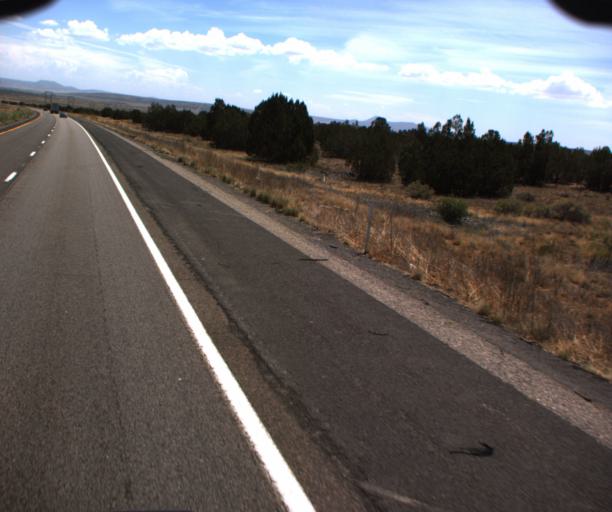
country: US
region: Arizona
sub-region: Mohave County
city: Peach Springs
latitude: 35.3025
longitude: -113.0041
